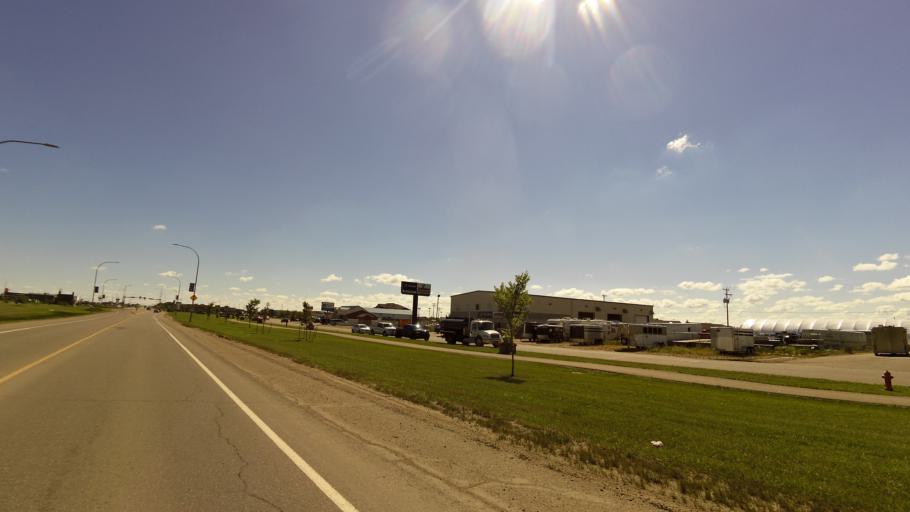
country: CA
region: Alberta
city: Wainwright
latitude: 52.8432
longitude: -110.8374
